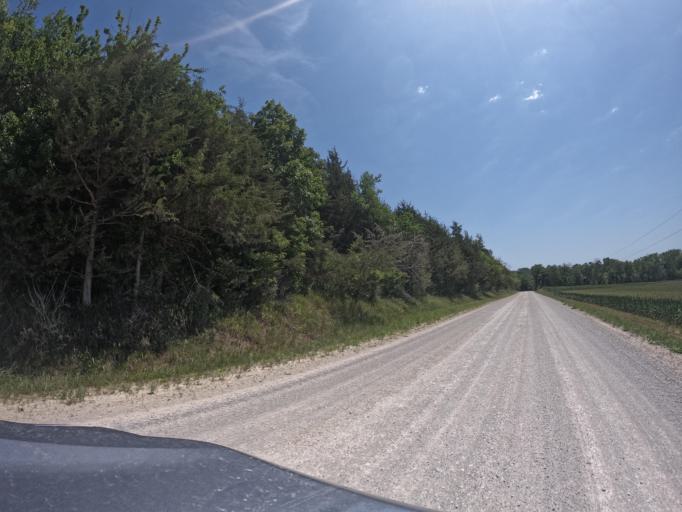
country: US
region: Iowa
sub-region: Henry County
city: Mount Pleasant
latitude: 40.8881
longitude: -91.5388
